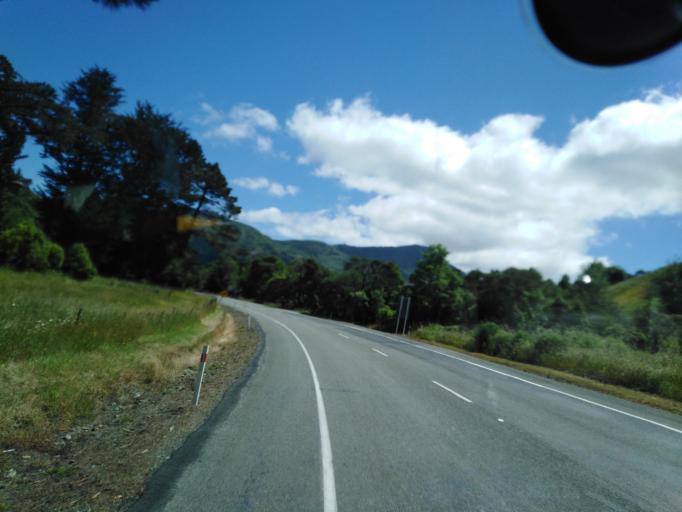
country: NZ
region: Nelson
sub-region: Nelson City
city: Nelson
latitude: -41.2199
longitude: 173.3979
